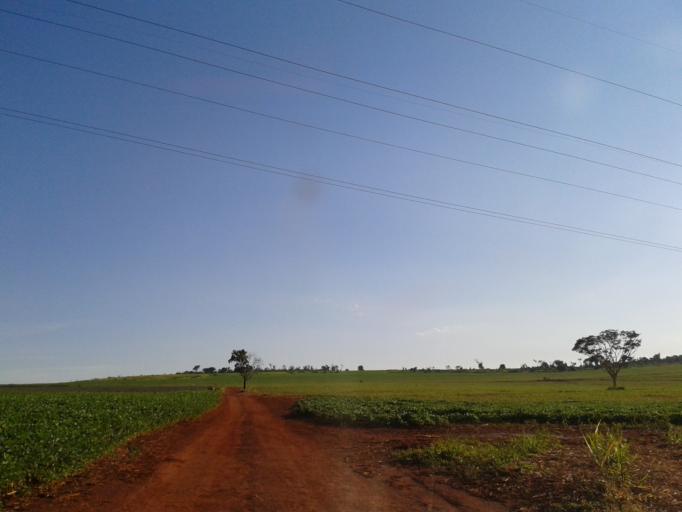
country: BR
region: Minas Gerais
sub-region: Centralina
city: Centralina
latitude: -18.6770
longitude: -49.2747
